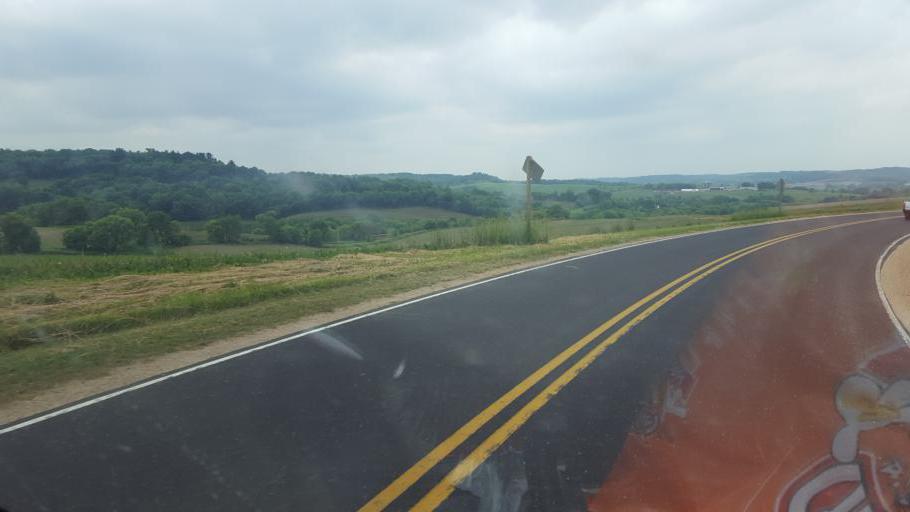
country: US
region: Wisconsin
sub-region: Vernon County
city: Hillsboro
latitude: 43.6507
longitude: -90.3158
